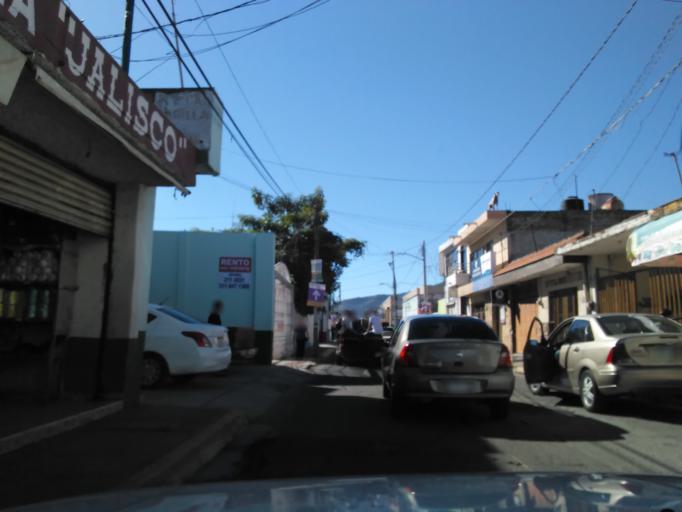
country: MX
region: Nayarit
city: Xalisco
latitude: 21.4468
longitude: -104.8996
